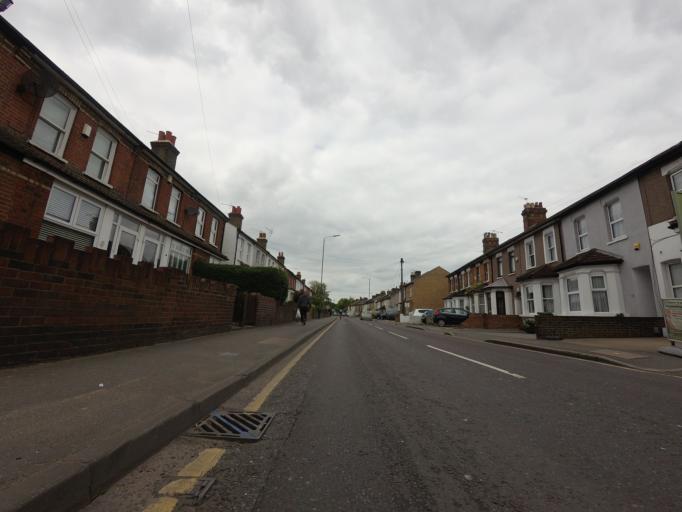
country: GB
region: England
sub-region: Greater London
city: Bexley
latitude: 51.4429
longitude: 0.1511
